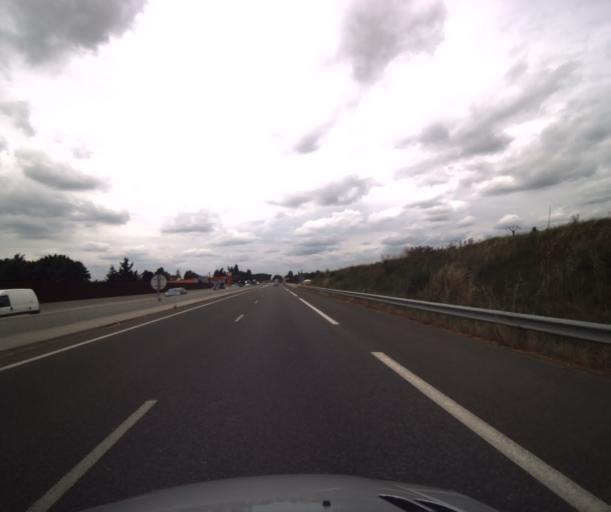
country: FR
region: Midi-Pyrenees
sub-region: Departement de la Haute-Garonne
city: Labarthe-sur-Leze
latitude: 43.4538
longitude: 1.4176
